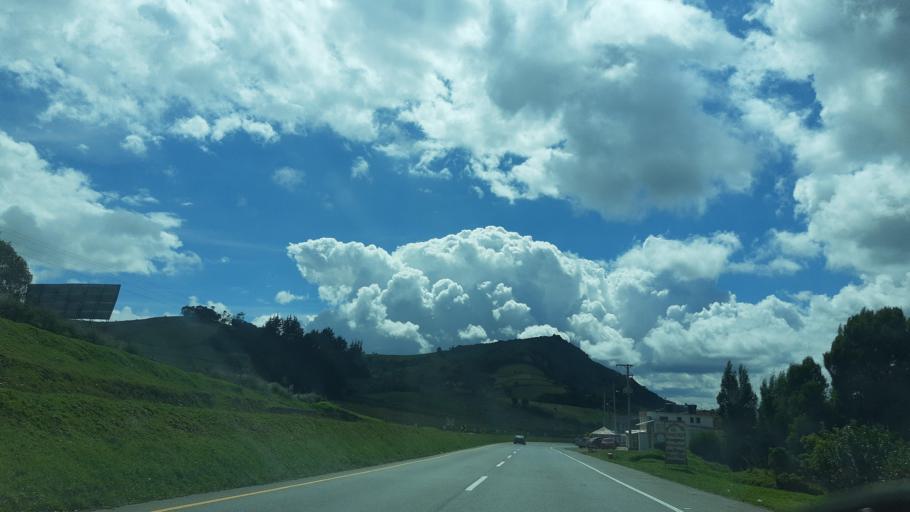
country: CO
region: Boyaca
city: Ventaquemada
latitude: 5.4136
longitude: -73.4616
